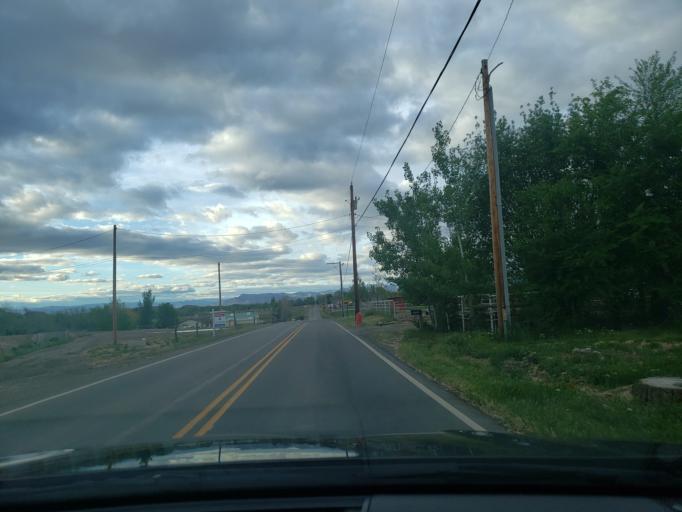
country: US
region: Colorado
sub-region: Mesa County
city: Fruita
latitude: 39.1818
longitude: -108.7290
